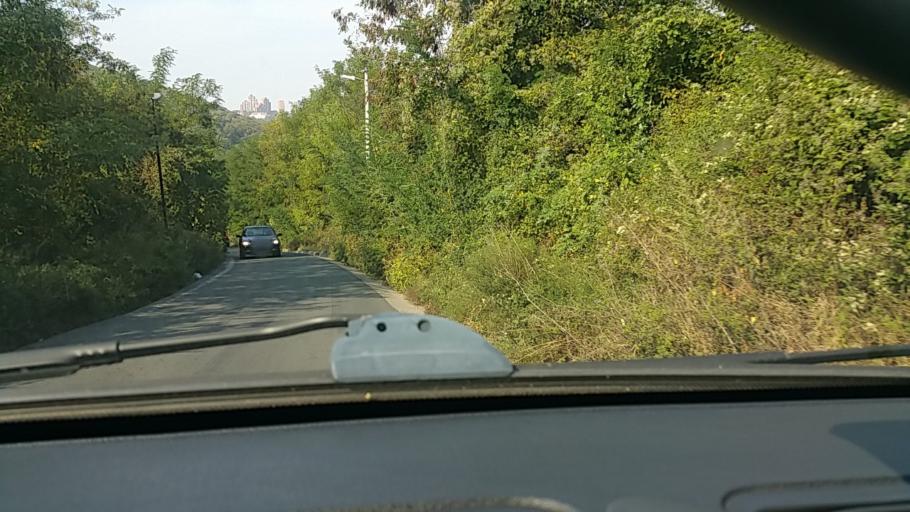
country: RS
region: Central Serbia
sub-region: Belgrade
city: Rakovica
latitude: 44.7354
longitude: 20.4522
